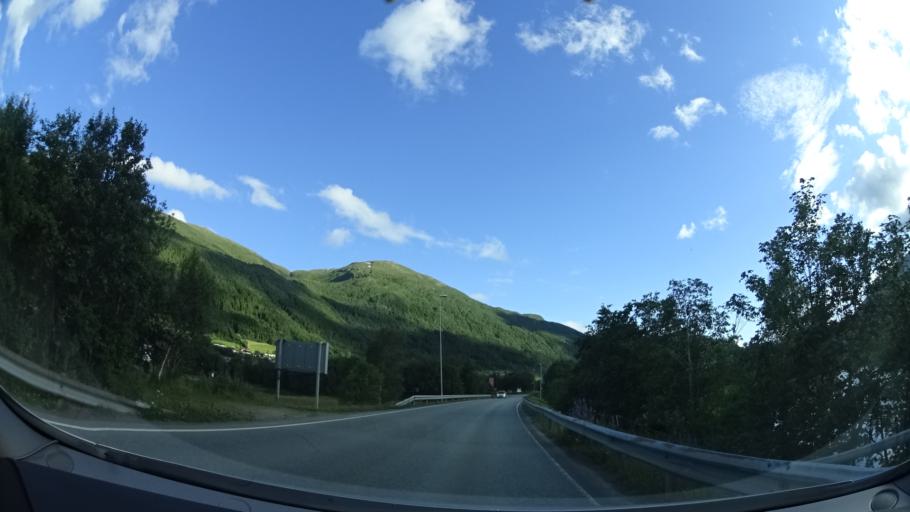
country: NO
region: More og Romsdal
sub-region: Gjemnes
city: Batnfjordsora
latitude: 62.8965
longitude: 7.6767
